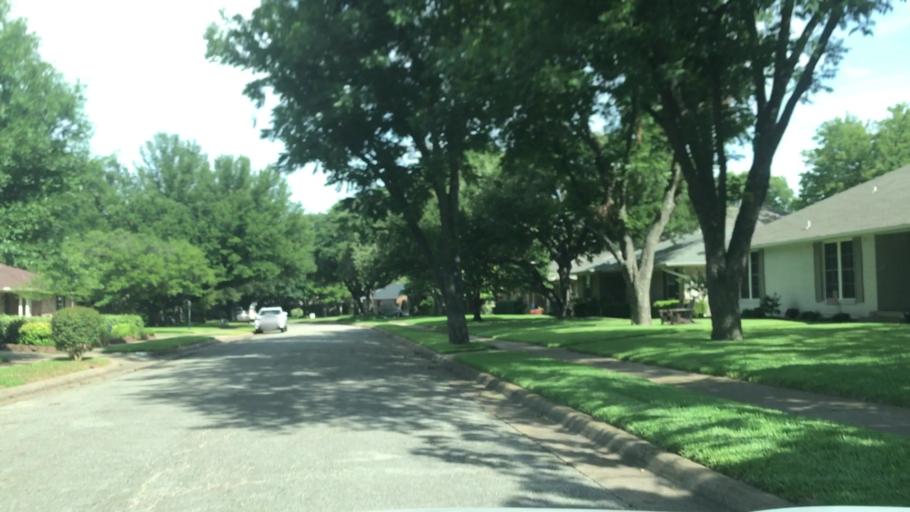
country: US
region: Texas
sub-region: Dallas County
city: Highland Park
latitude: 32.8542
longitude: -96.7567
